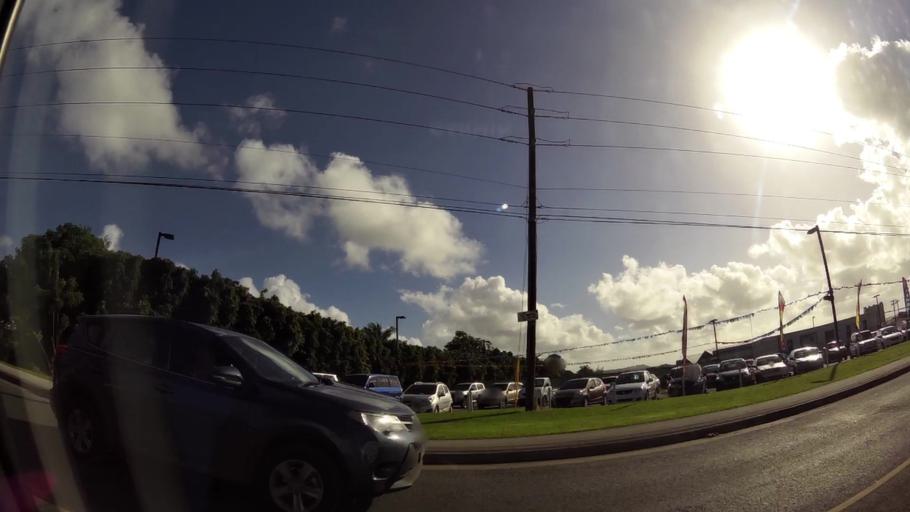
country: BB
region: Saint Michael
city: Bridgetown
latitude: 13.1469
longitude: -59.6104
